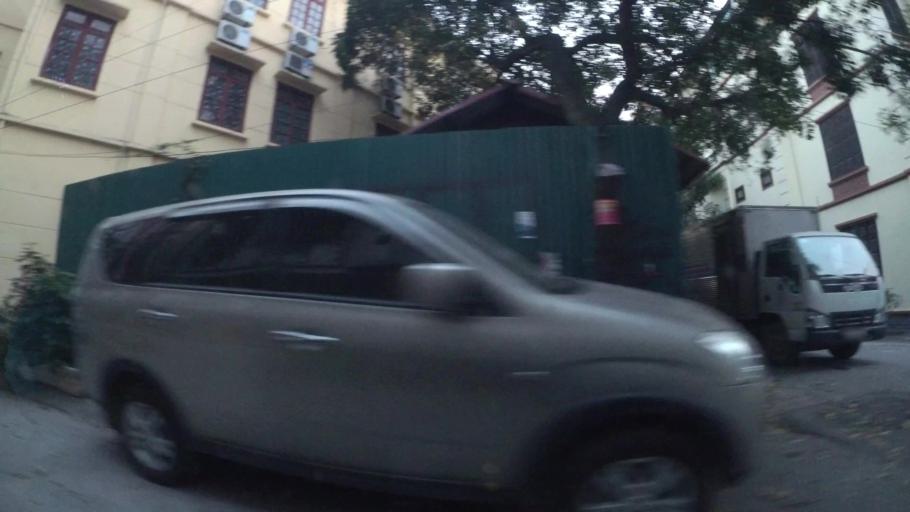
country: VN
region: Ha Noi
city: Ha Dong
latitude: 20.9722
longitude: 105.7873
